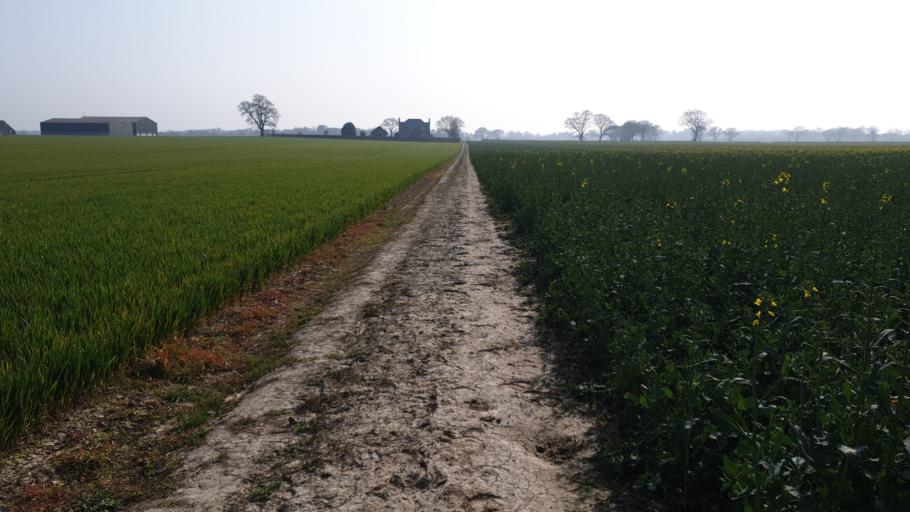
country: GB
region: England
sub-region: Essex
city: Mistley
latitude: 51.8945
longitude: 1.1209
